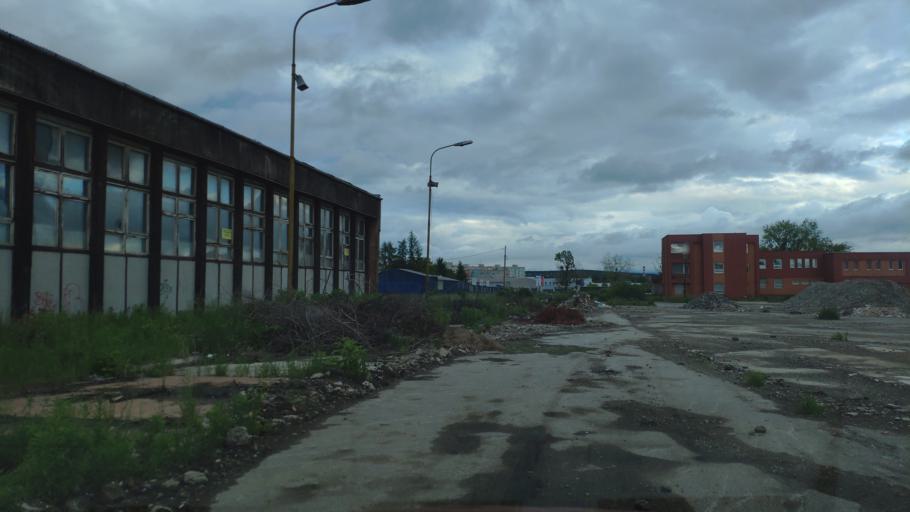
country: SK
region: Kosicky
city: Kosice
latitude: 48.6987
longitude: 21.2450
